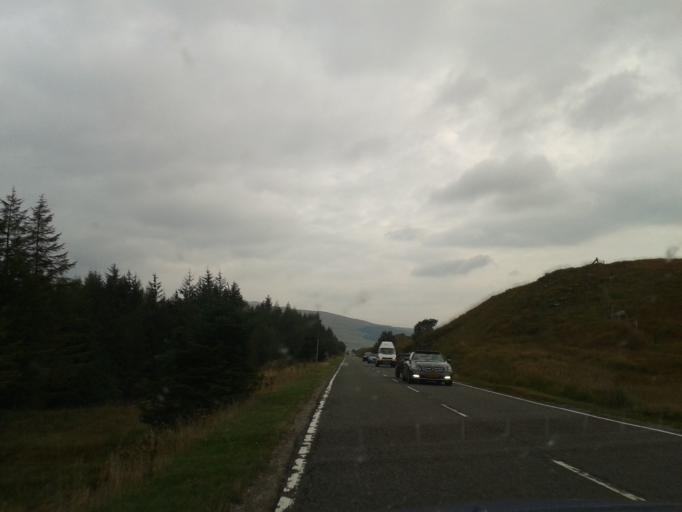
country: GB
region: Scotland
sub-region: Highland
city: Spean Bridge
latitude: 56.5422
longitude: -4.7635
